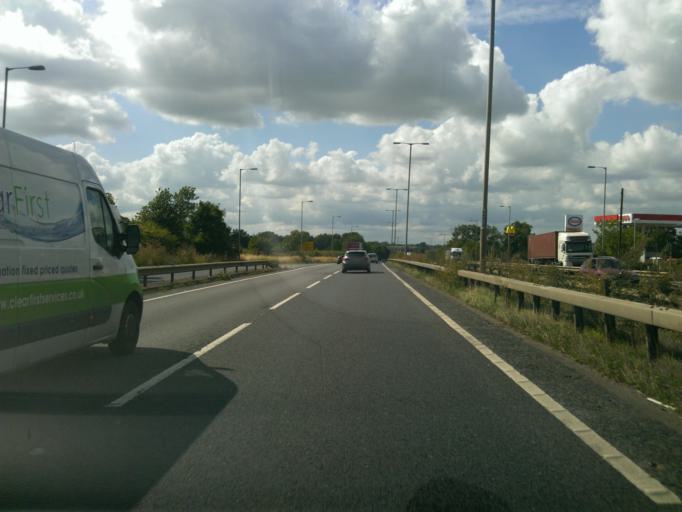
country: GB
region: England
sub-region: Northamptonshire
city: Rothwell
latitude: 52.4139
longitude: -0.7893
